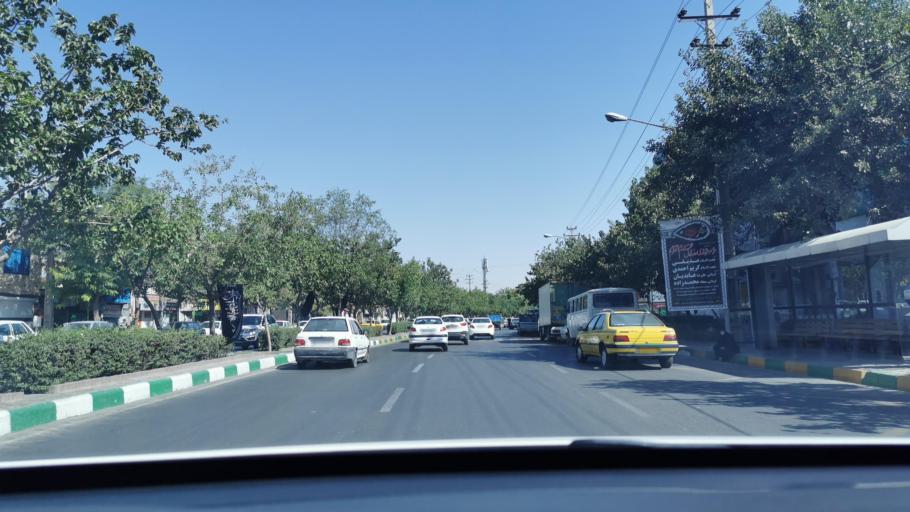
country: IR
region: Razavi Khorasan
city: Mashhad
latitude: 36.3393
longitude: 59.6251
